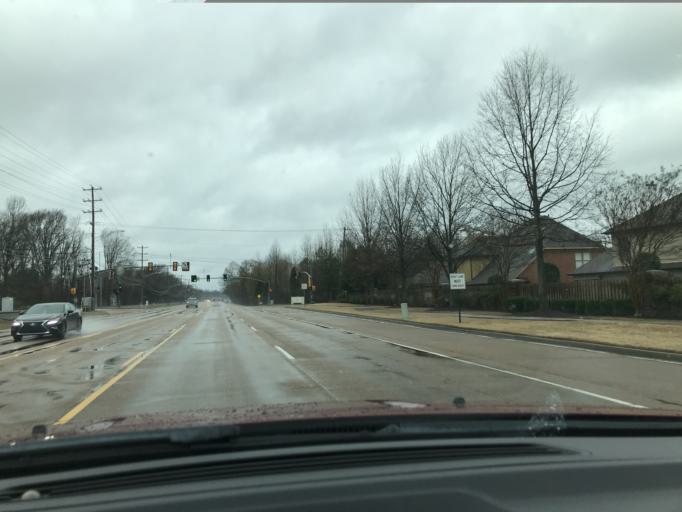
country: US
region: Tennessee
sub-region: Shelby County
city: Collierville
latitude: 35.0488
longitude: -89.7230
